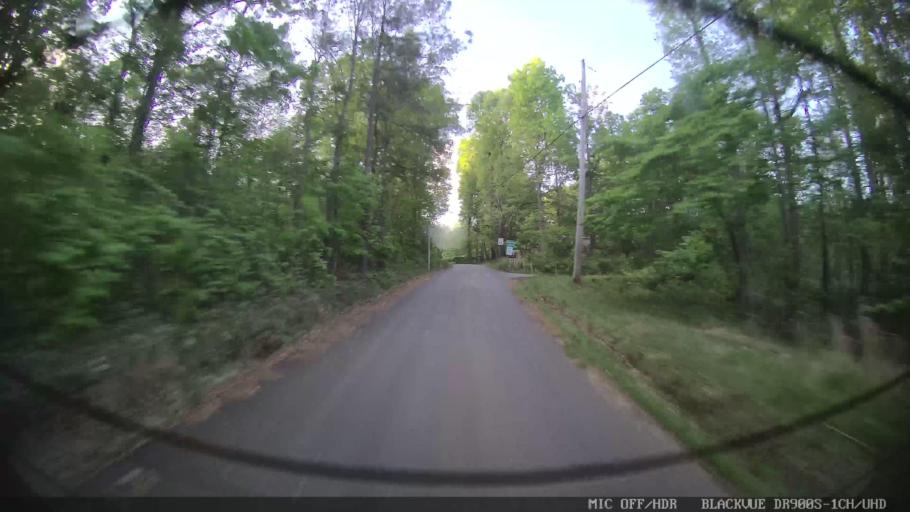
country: US
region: Georgia
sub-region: Bartow County
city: Emerson
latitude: 34.0823
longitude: -84.7720
